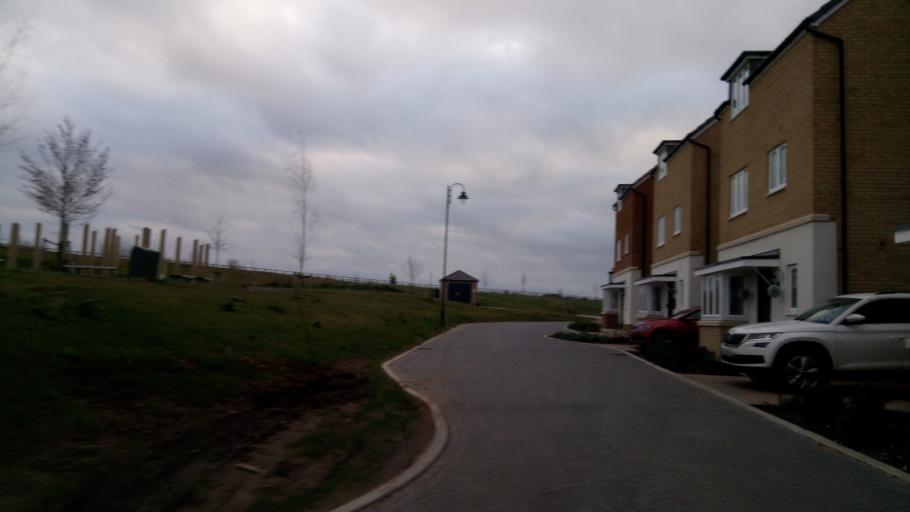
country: GB
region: England
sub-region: Cambridgeshire
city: Yaxley
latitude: 52.5280
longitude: -0.2840
